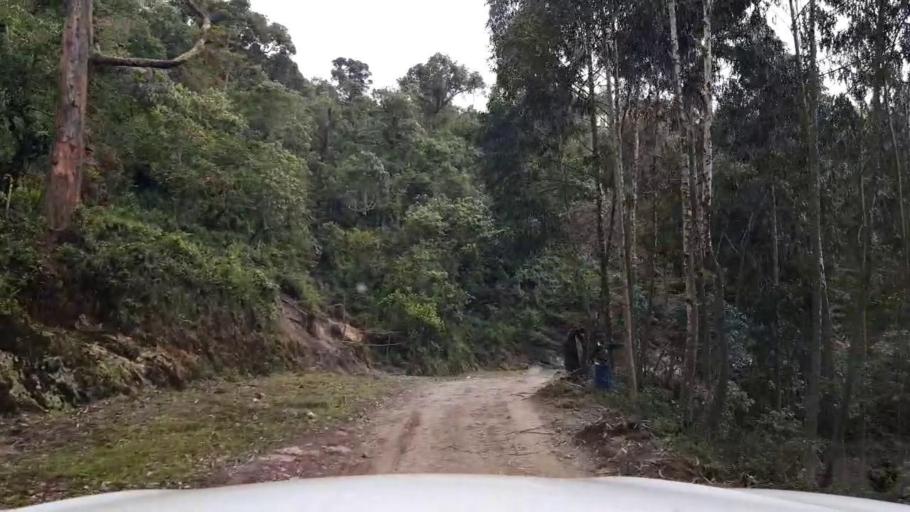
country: RW
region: Western Province
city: Kibuye
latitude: -1.9686
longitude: 29.4870
